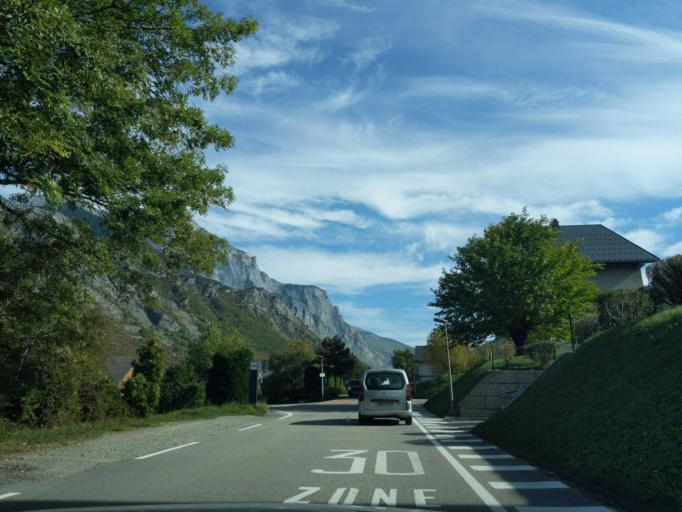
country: FR
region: Rhone-Alpes
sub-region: Departement de la Savoie
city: Villargondran
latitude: 45.2639
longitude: 6.3774
